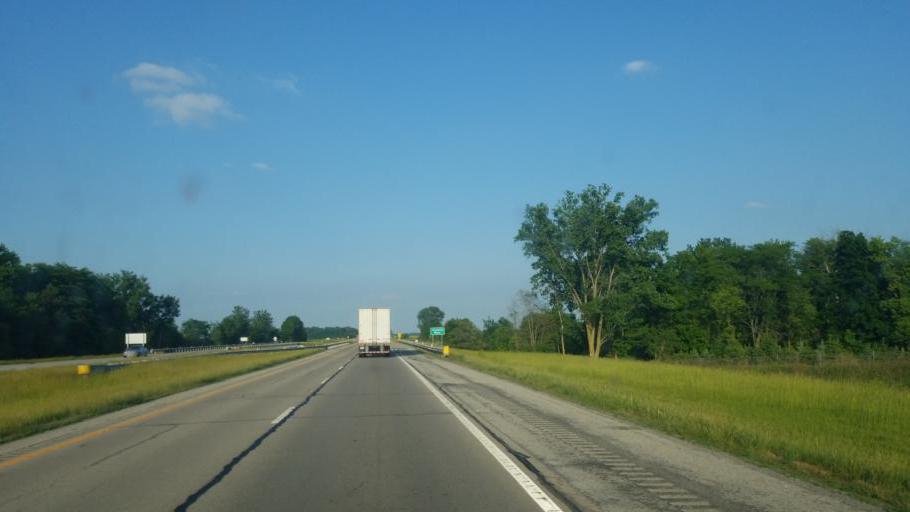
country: US
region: Ohio
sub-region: Allen County
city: Delphos
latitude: 40.8375
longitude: -84.2891
